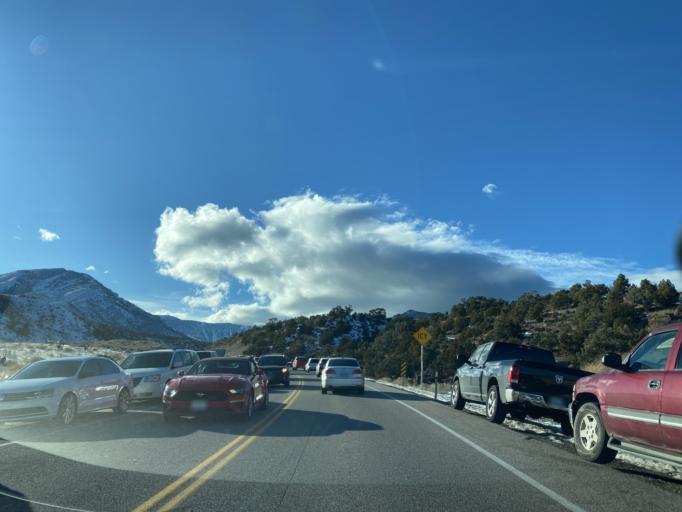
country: US
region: Nevada
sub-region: Clark County
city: Summerlin South
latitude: 36.2718
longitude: -115.5392
